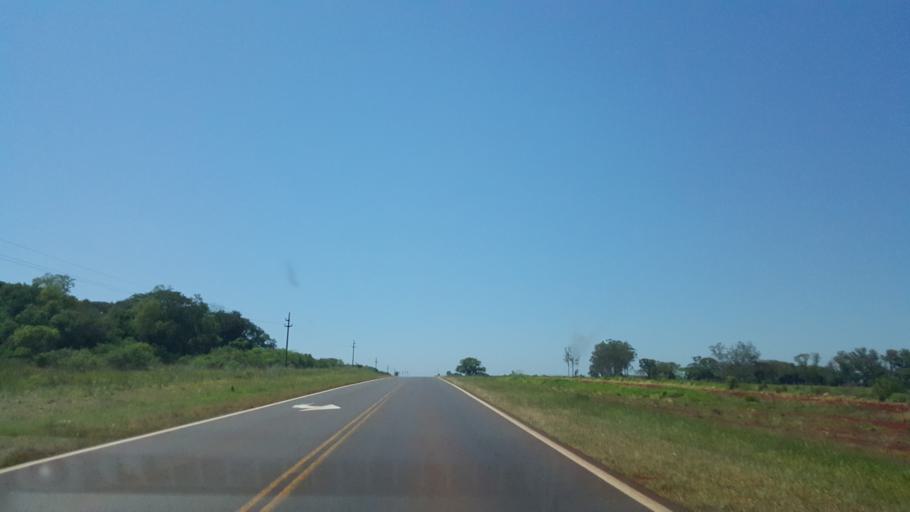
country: AR
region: Corrientes
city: Santo Tome
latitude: -28.3650
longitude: -56.1111
